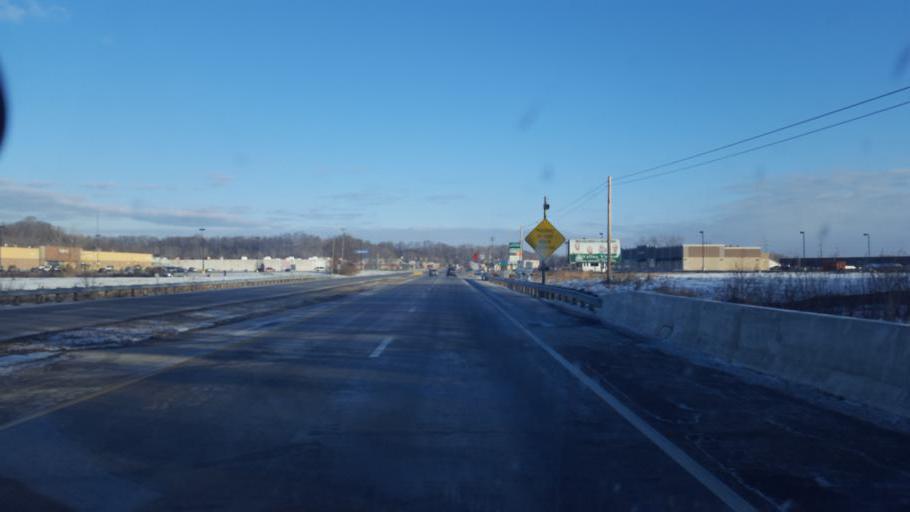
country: US
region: Ohio
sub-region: Pike County
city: Waverly
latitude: 39.1078
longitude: -82.9978
